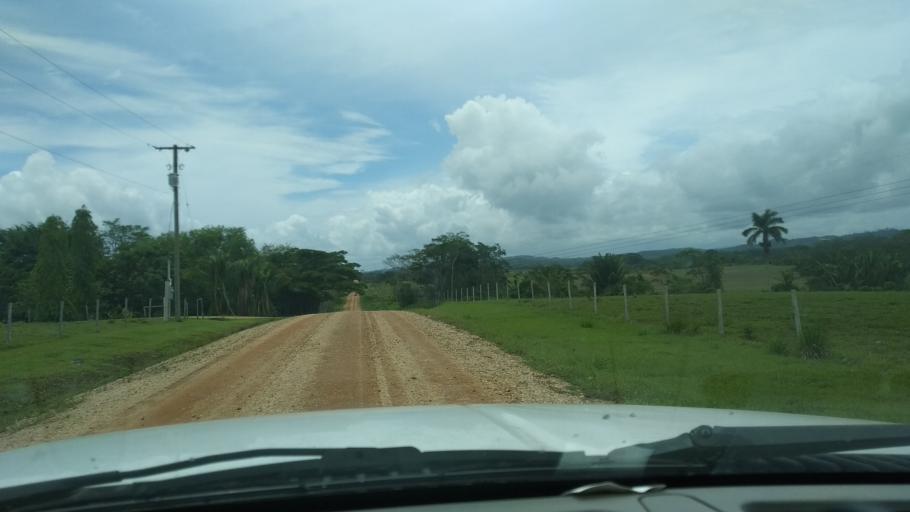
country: BZ
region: Cayo
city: San Ignacio
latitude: 17.2263
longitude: -88.9851
